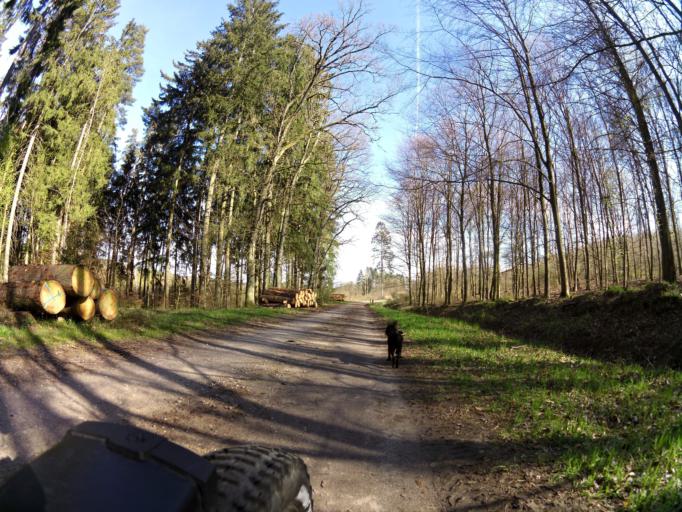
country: PL
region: West Pomeranian Voivodeship
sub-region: Powiat lobeski
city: Lobez
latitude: 53.7687
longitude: 15.5853
